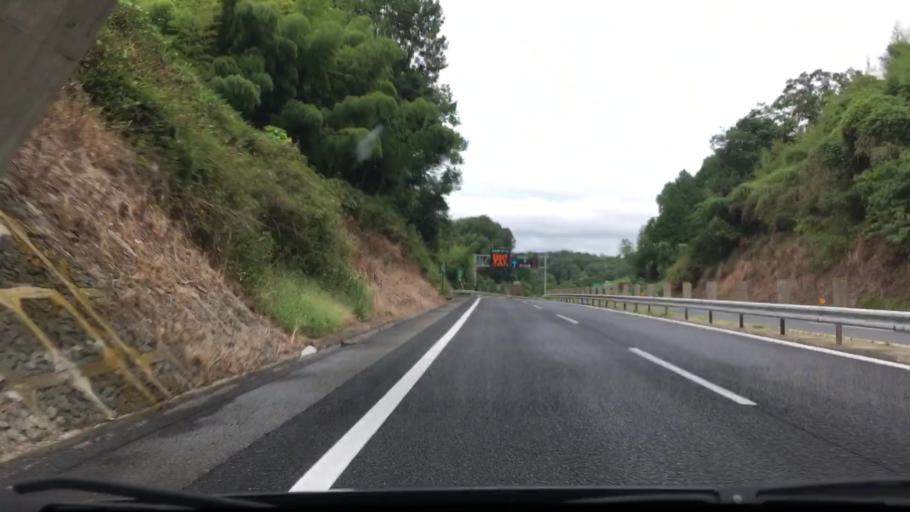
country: JP
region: Hiroshima
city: Miyoshi
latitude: 34.8063
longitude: 132.9198
